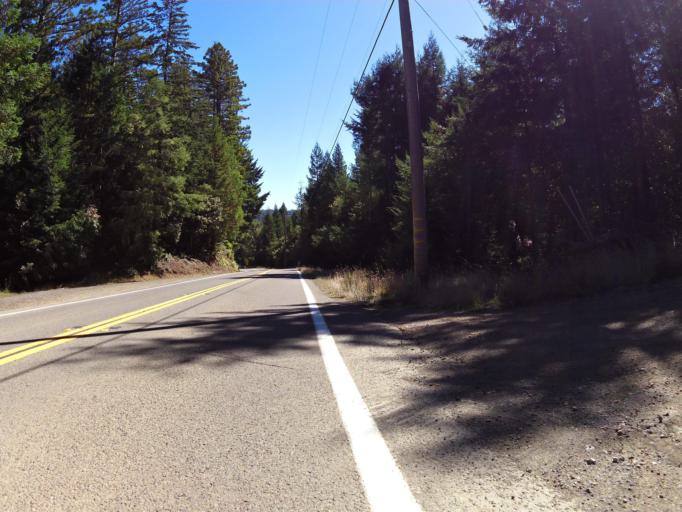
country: US
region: California
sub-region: Mendocino County
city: Fort Bragg
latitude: 39.7221
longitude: -123.8075
